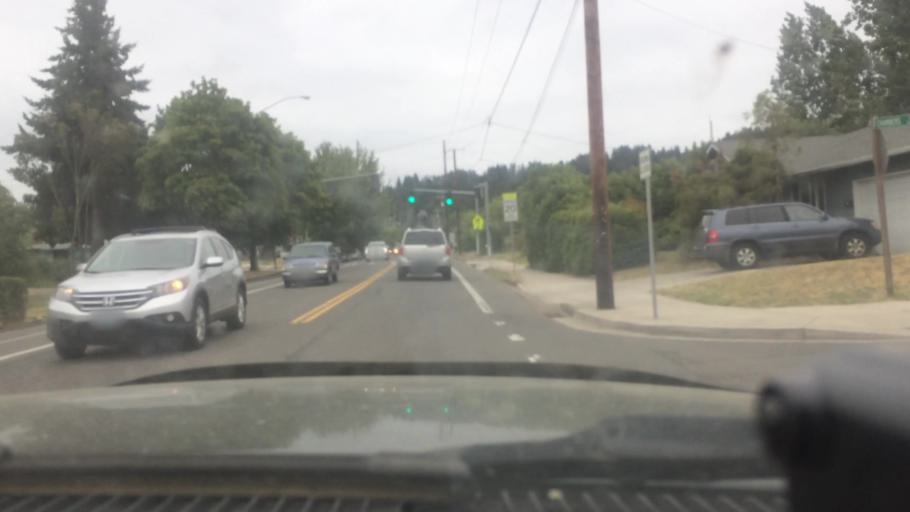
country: US
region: Oregon
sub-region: Lane County
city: Eugene
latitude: 44.0363
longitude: -123.1179
